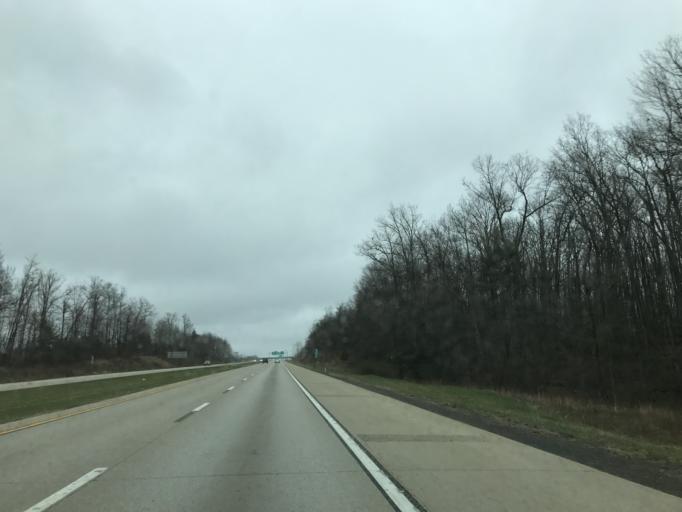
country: US
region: West Virginia
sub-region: Raleigh County
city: Daniels
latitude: 37.7735
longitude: -81.0794
